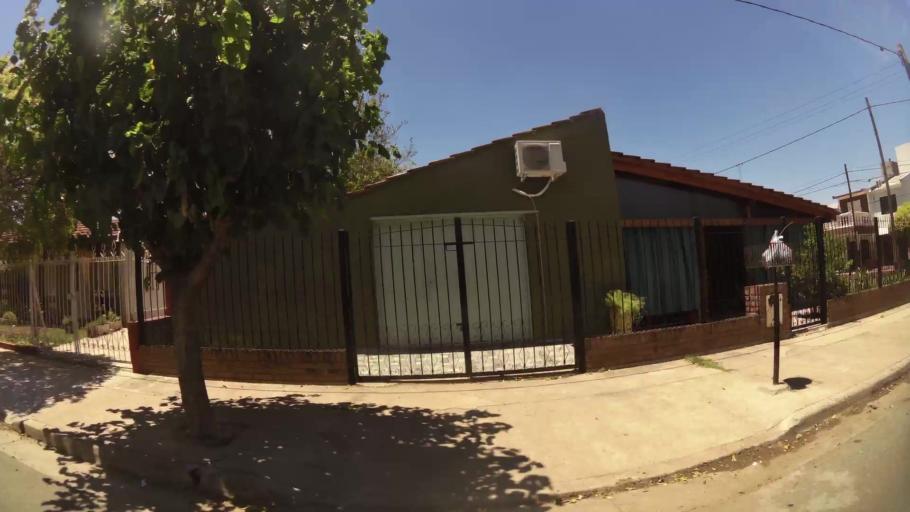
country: AR
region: Cordoba
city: Malvinas Argentinas
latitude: -31.3793
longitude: -64.1286
